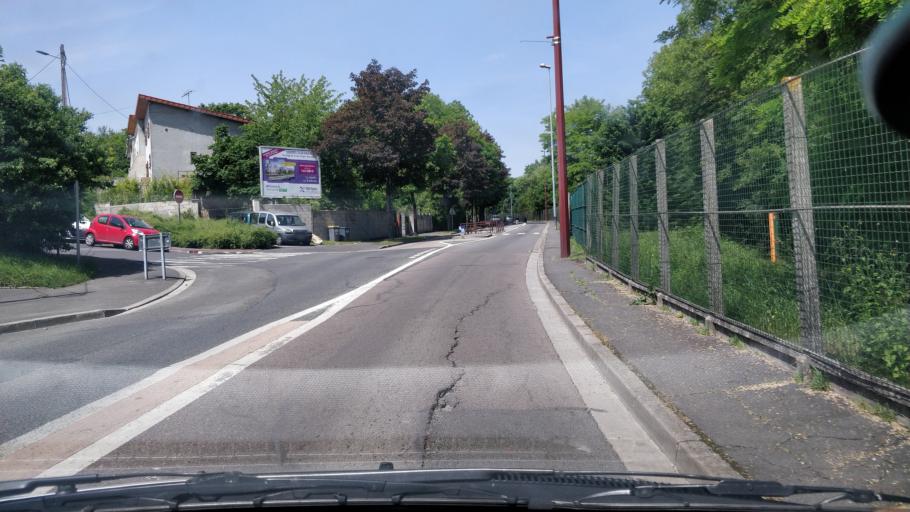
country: FR
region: Ile-de-France
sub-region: Departement de Seine-Saint-Denis
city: Montfermeil
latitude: 48.8955
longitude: 2.5681
